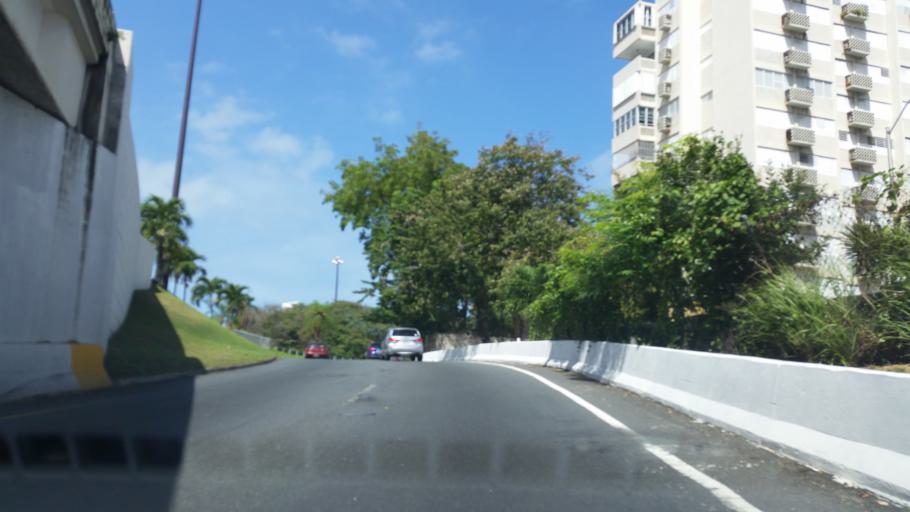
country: PR
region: San Juan
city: San Juan
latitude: 18.4505
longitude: -66.0667
